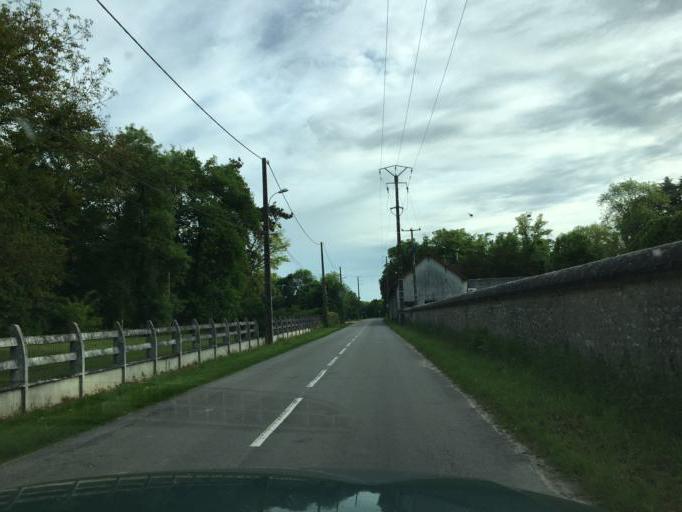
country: FR
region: Centre
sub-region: Departement du Loiret
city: Saint-Ay
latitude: 47.8698
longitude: 1.7417
